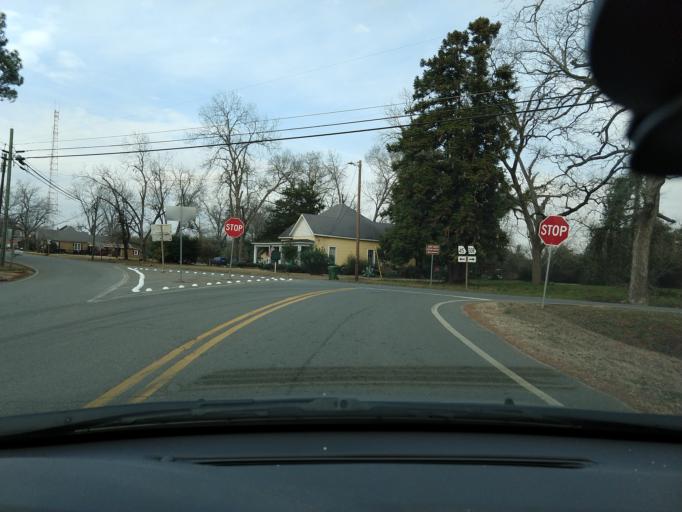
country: US
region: Georgia
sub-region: Webster County
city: Preston
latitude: 32.0303
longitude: -84.3913
